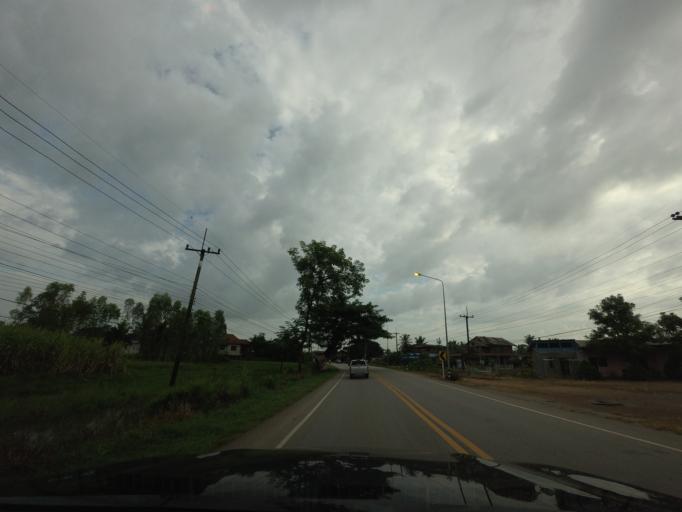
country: TH
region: Changwat Udon Thani
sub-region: Amphoe Ban Phue
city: Ban Phue
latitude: 17.7434
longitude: 102.3989
